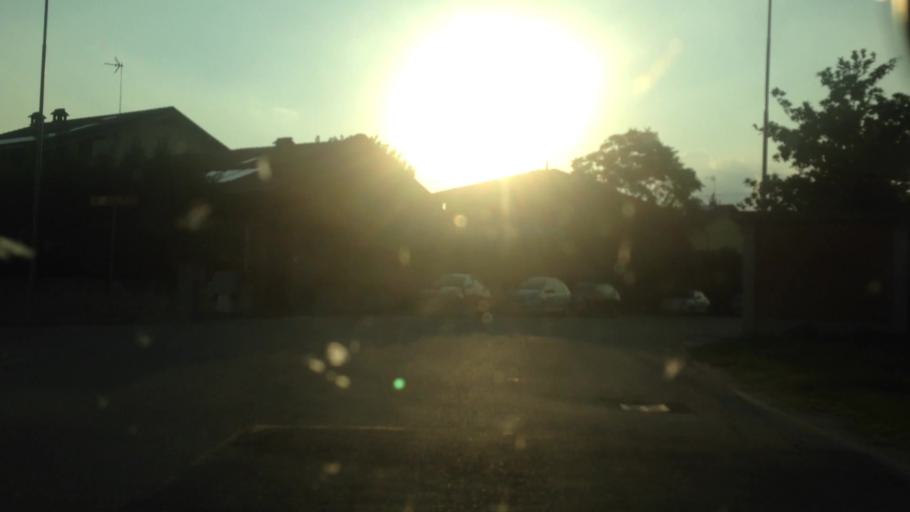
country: IT
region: Piedmont
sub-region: Provincia di Asti
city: Asti
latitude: 44.9164
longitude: 8.2266
